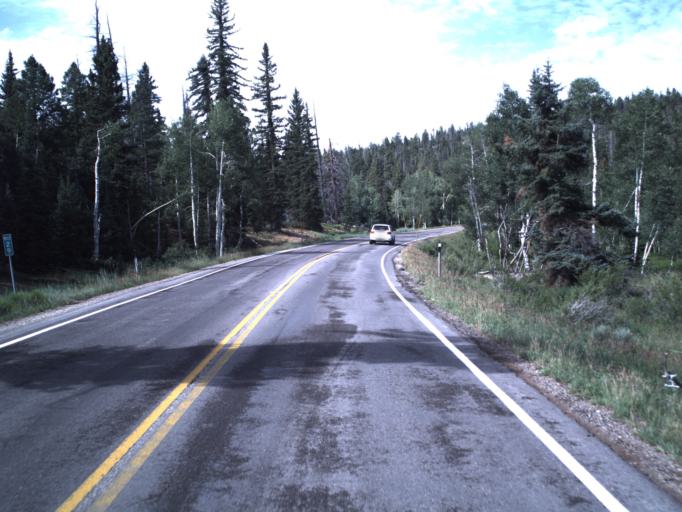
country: US
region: Utah
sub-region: Iron County
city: Parowan
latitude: 37.5152
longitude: -112.6842
